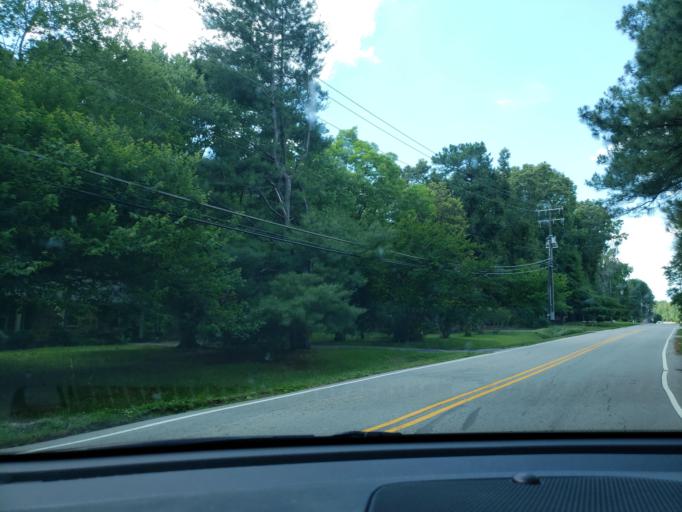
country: US
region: North Carolina
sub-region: Orange County
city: Chapel Hill
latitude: 35.9760
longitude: -78.9902
